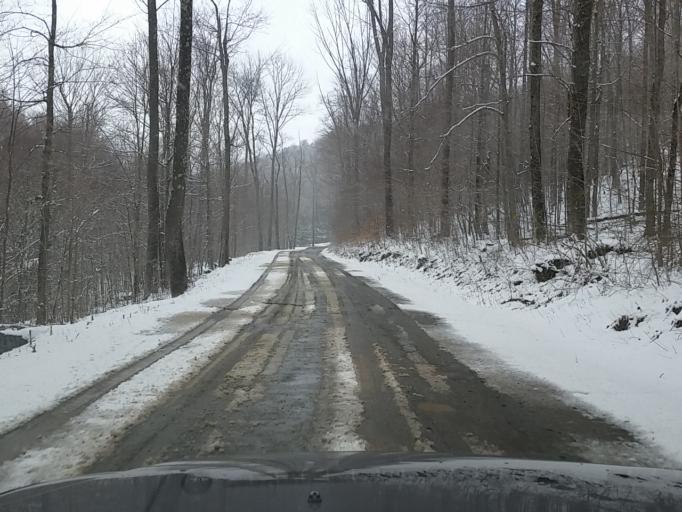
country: US
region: Pennsylvania
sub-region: Sullivan County
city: Laporte
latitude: 41.3319
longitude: -76.4610
